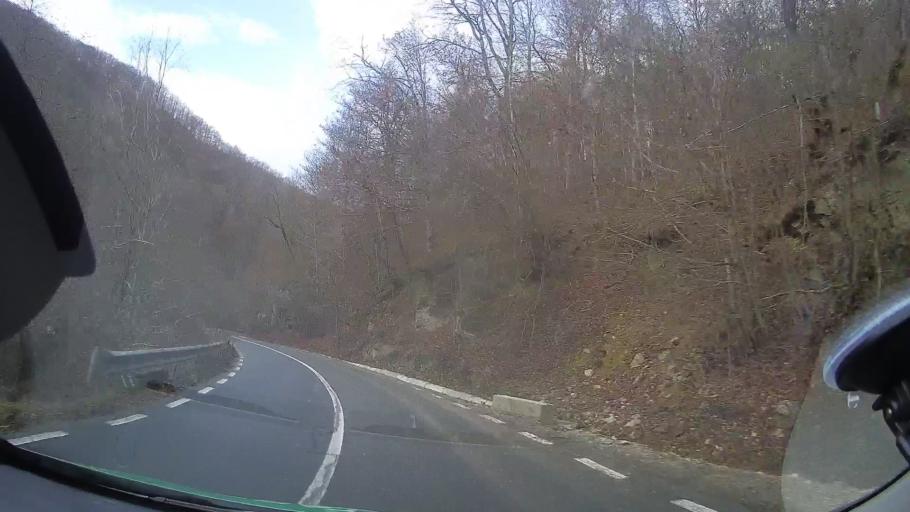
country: RO
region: Cluj
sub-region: Comuna Valea Ierii
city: Valea Ierii
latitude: 46.6304
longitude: 23.3764
